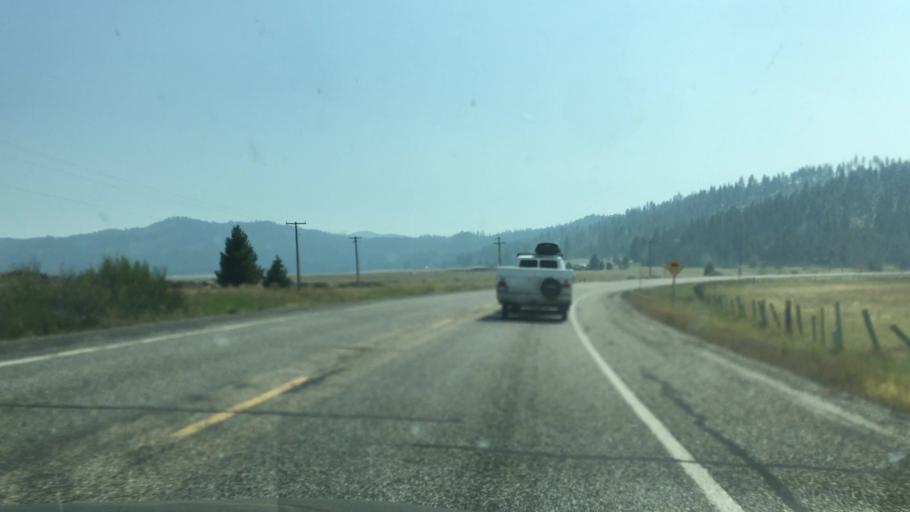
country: US
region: Idaho
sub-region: Valley County
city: Cascade
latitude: 44.3388
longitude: -116.0301
